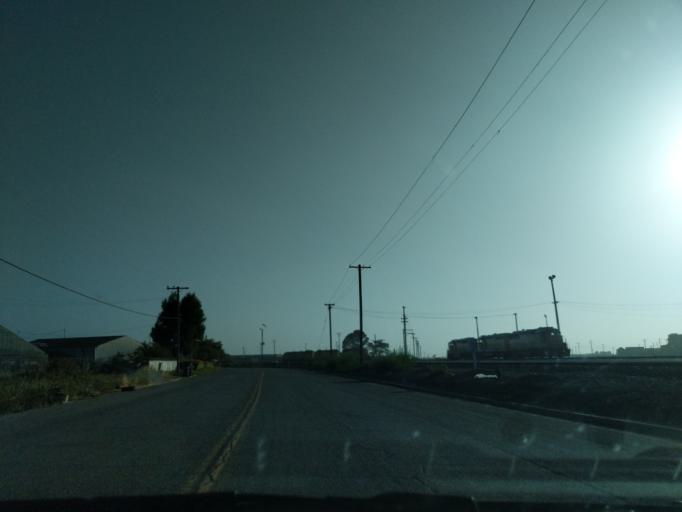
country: US
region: California
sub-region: Monterey County
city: Pajaro
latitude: 36.8956
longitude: -121.7429
